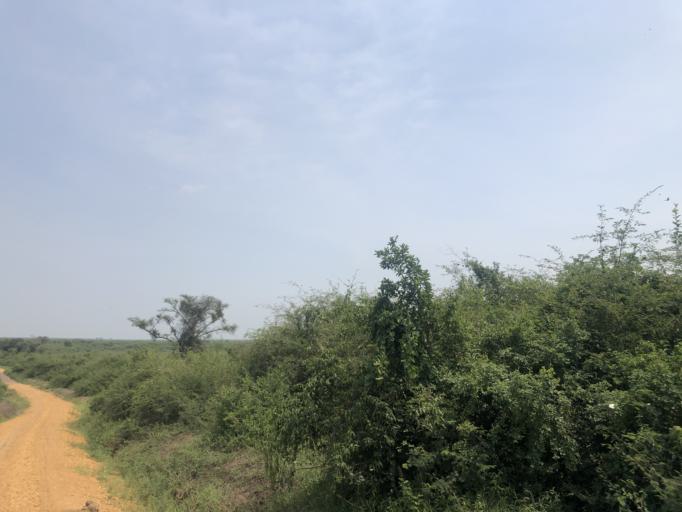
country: UG
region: Western Region
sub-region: Rubirizi District
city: Rubirizi
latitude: -0.2125
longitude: 29.9514
